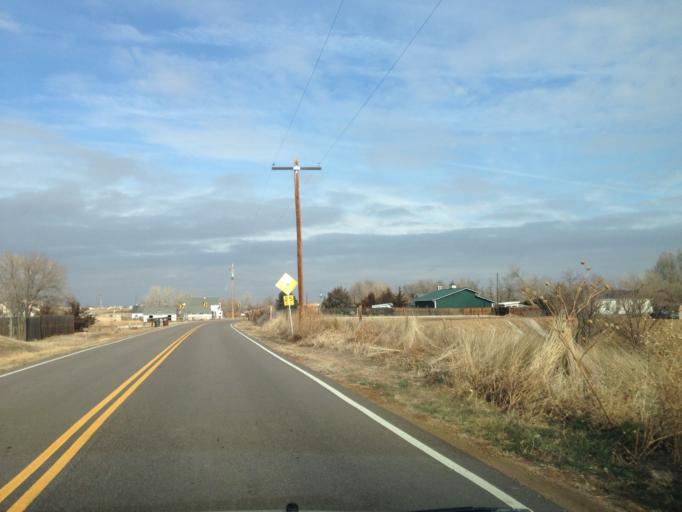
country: US
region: Colorado
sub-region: Boulder County
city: Lafayette
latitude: 39.9966
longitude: -105.0606
